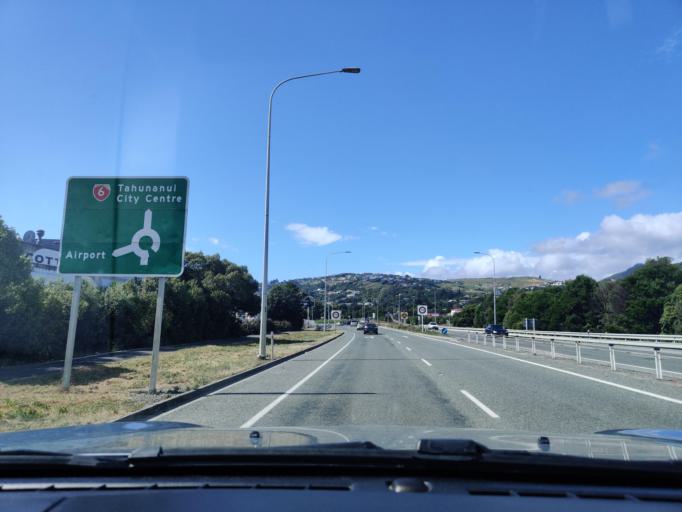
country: NZ
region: Nelson
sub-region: Nelson City
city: Nelson
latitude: -41.3012
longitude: 173.2384
